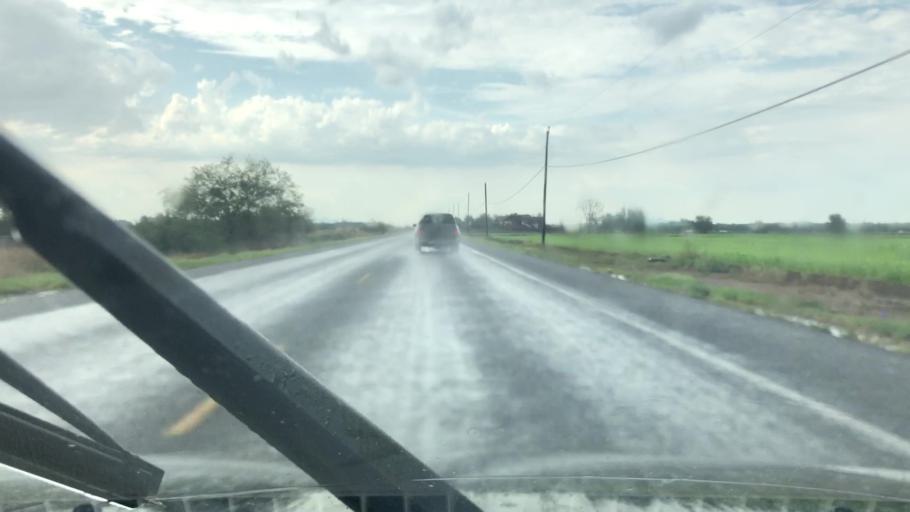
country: US
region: New Mexico
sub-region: Dona Ana County
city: Mesquite
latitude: 32.1841
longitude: -106.7089
